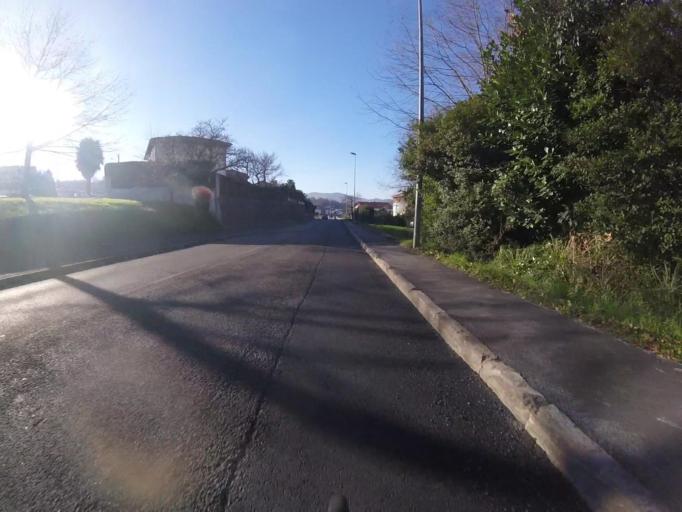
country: FR
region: Aquitaine
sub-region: Departement des Pyrenees-Atlantiques
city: Hendaye
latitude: 43.3611
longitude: -1.7624
